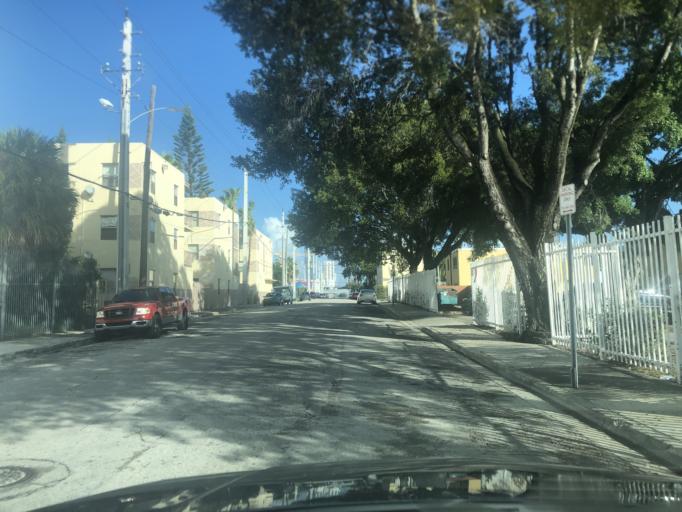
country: US
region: Florida
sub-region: Miami-Dade County
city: Miami
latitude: 25.7976
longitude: -80.2015
